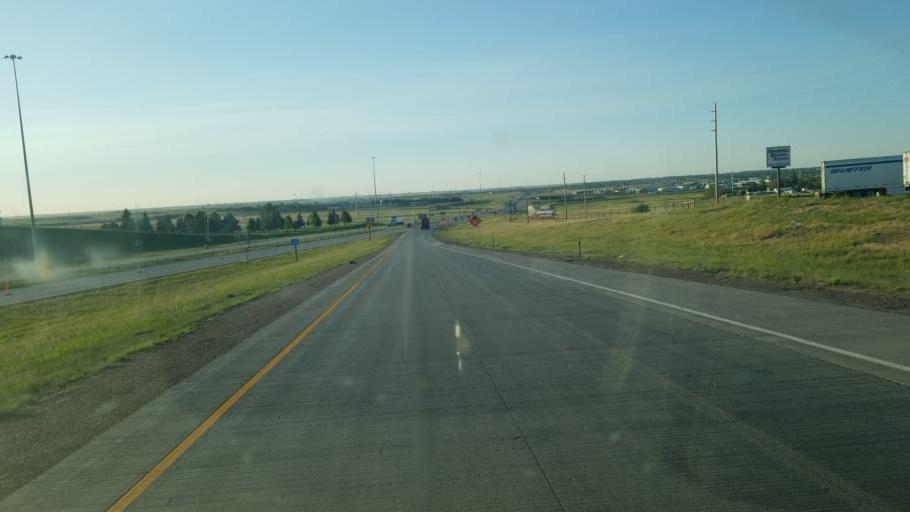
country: US
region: Wyoming
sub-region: Laramie County
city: South Greeley
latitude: 41.1007
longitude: -104.8497
